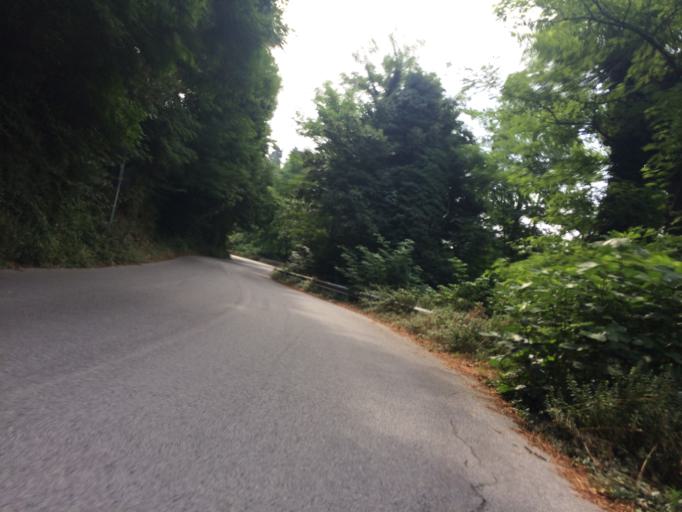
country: IT
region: Liguria
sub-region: Provincia di Savona
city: San Giovanni
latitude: 44.4015
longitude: 8.4920
